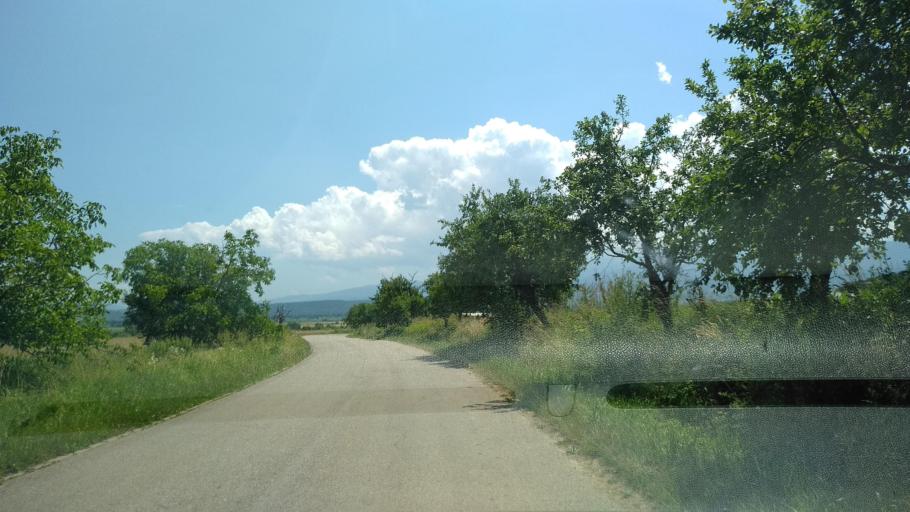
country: RO
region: Hunedoara
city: Densus
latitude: 45.5611
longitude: 22.8169
